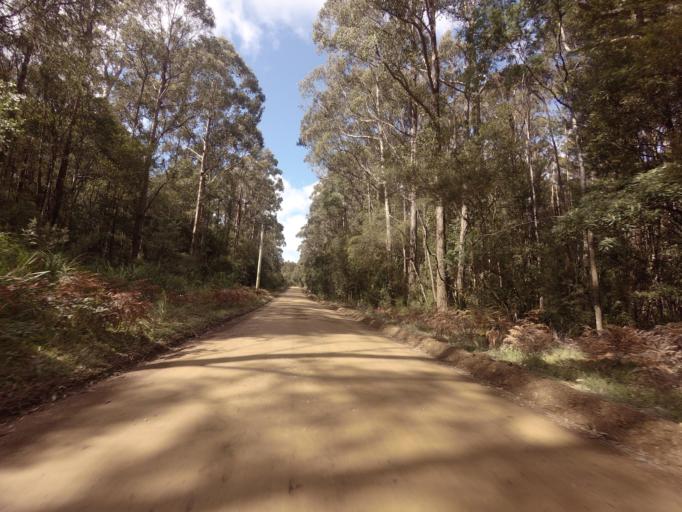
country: AU
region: Tasmania
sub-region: Huon Valley
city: Geeveston
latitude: -43.4130
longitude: 146.8997
